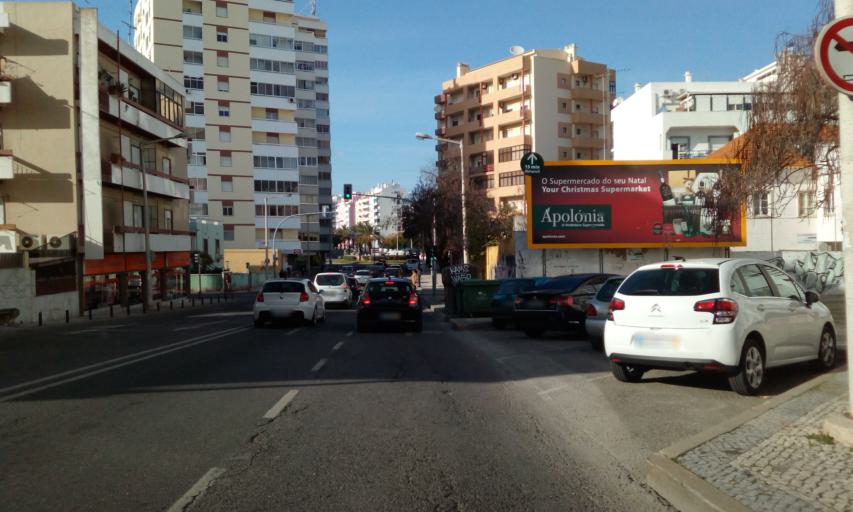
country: PT
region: Faro
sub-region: Faro
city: Faro
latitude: 37.0230
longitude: -7.9252
